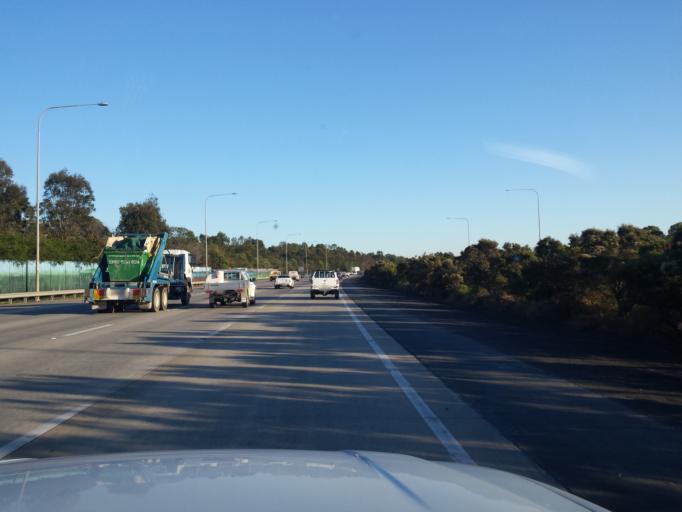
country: AU
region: Queensland
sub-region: Gold Coast
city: Ormeau Hills
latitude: -27.7839
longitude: 153.2545
